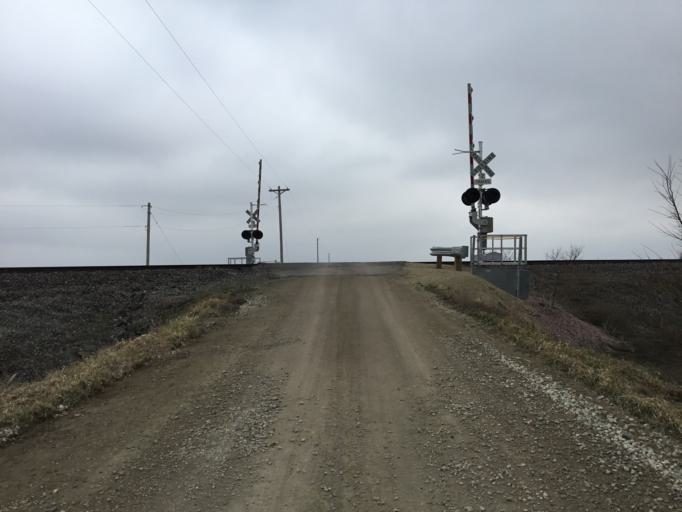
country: US
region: Kansas
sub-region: Dickinson County
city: Herington
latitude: 38.7165
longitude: -96.8905
